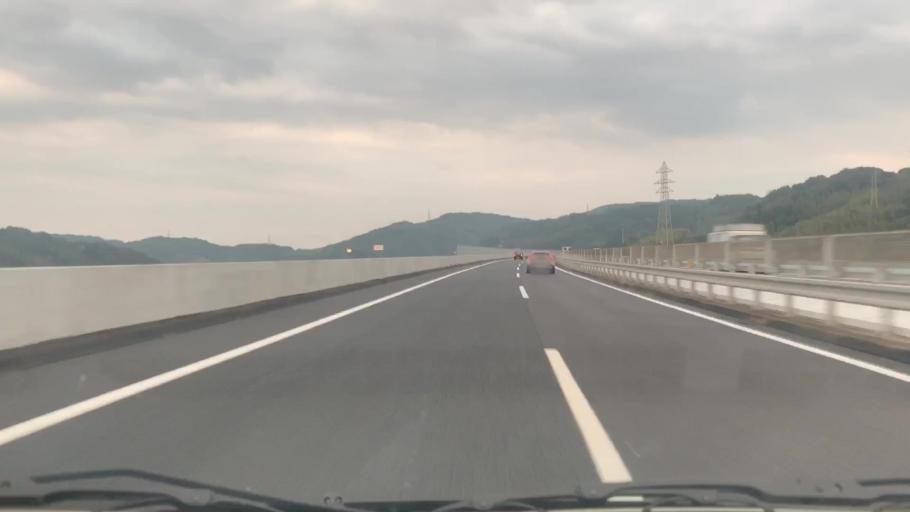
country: JP
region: Nagasaki
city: Omura
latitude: 32.8904
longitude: 129.9895
